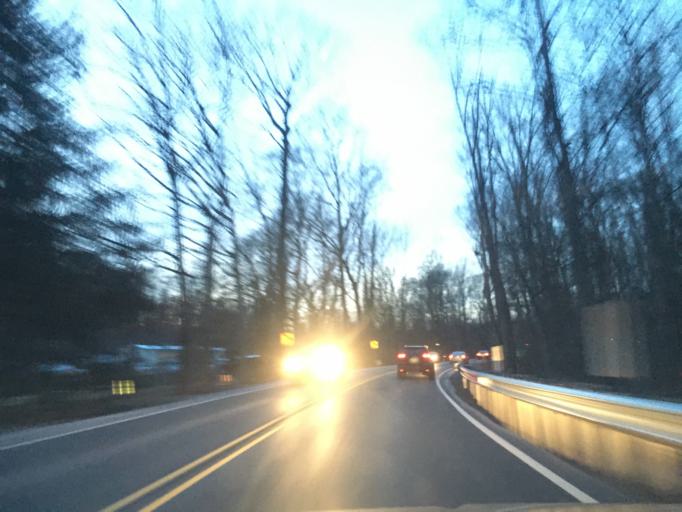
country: US
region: Pennsylvania
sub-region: Northampton County
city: Cherryville
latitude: 40.7486
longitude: -75.5211
